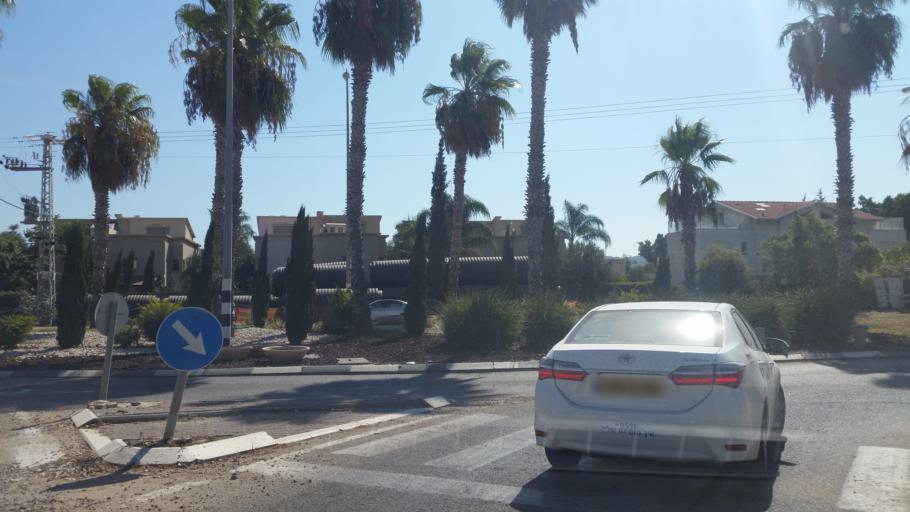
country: IL
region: Haifa
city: `Atlit
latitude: 32.6923
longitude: 34.9452
